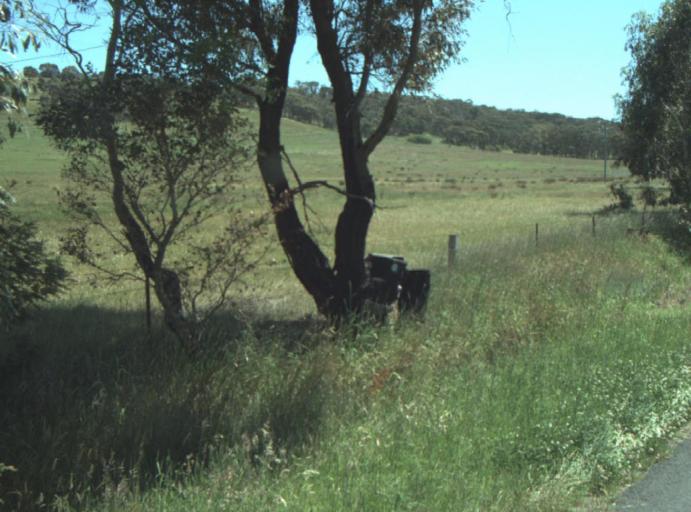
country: AU
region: Victoria
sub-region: Greater Geelong
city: Lara
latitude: -37.8909
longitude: 144.2559
